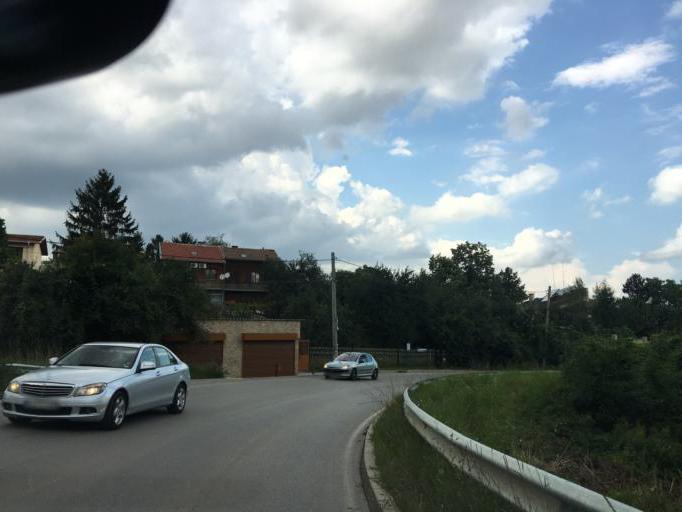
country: BG
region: Sofia-Capital
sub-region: Stolichna Obshtina
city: Sofia
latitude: 42.6179
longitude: 23.3583
